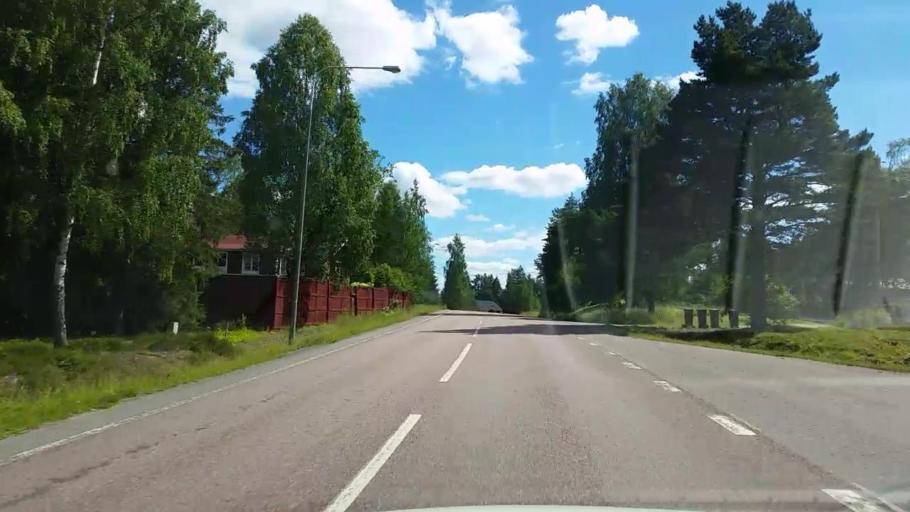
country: SE
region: Dalarna
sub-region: Faluns Kommun
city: Svardsjo
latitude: 60.8283
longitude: 15.7604
